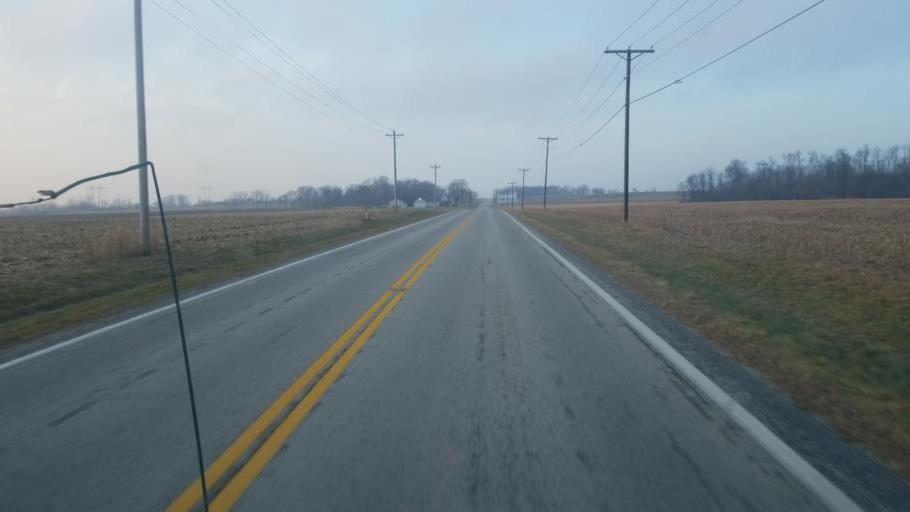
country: US
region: Ohio
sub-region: Wyandot County
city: Carey
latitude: 41.0024
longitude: -83.2745
